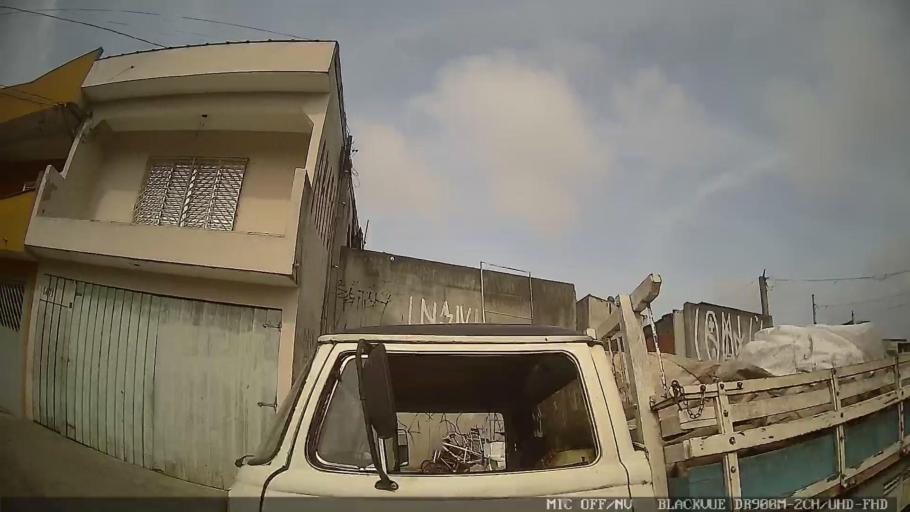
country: BR
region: Sao Paulo
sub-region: Itaquaquecetuba
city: Itaquaquecetuba
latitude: -23.4997
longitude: -46.3676
